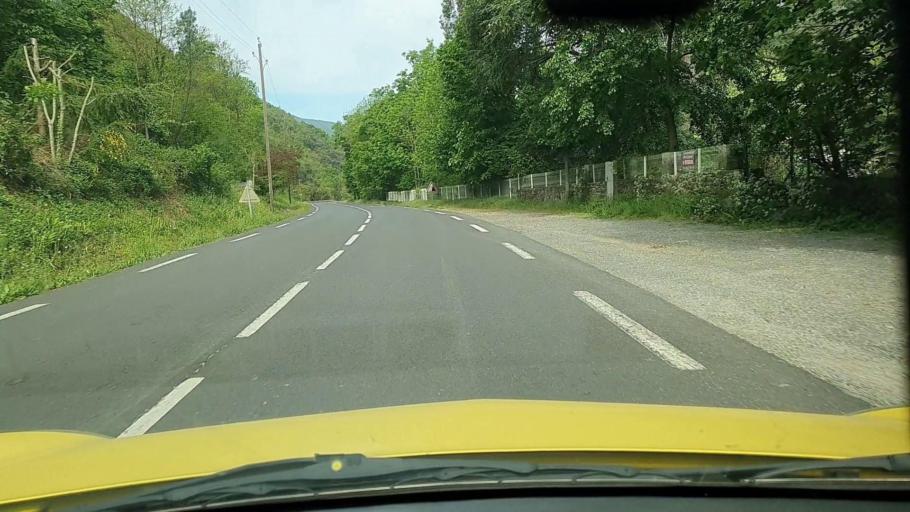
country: FR
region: Languedoc-Roussillon
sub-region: Departement du Gard
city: Valleraugue
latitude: 44.0775
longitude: 3.6589
